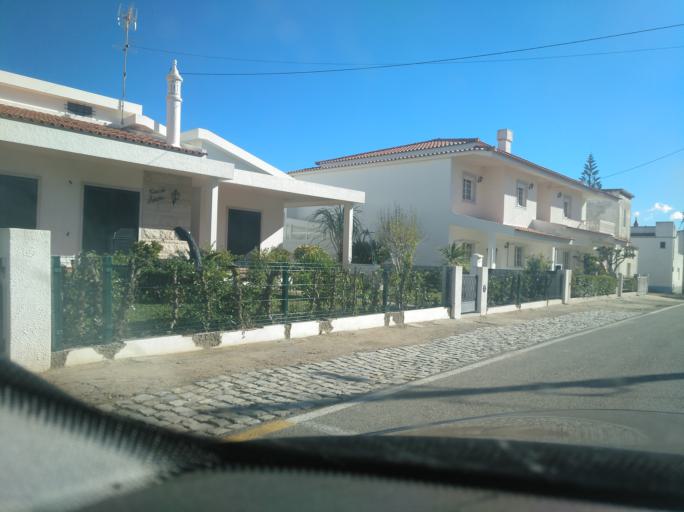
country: PT
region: Faro
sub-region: Vila Real de Santo Antonio
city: Monte Gordo
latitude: 37.1691
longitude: -7.5237
